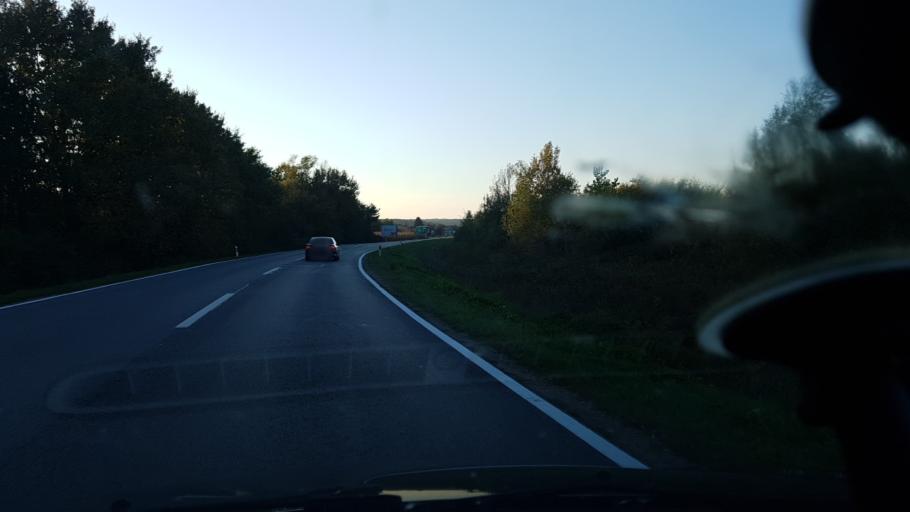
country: HR
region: Koprivnicko-Krizevacka
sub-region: Grad Koprivnica
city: Koprivnica
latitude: 46.1454
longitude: 16.8223
